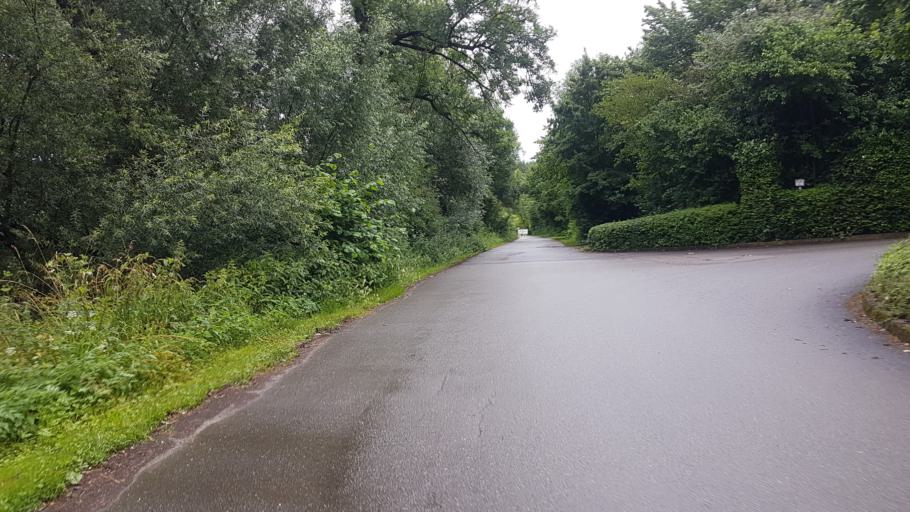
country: DE
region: Baden-Wuerttemberg
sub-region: Tuebingen Region
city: Rottenacker
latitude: 48.2365
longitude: 9.7044
